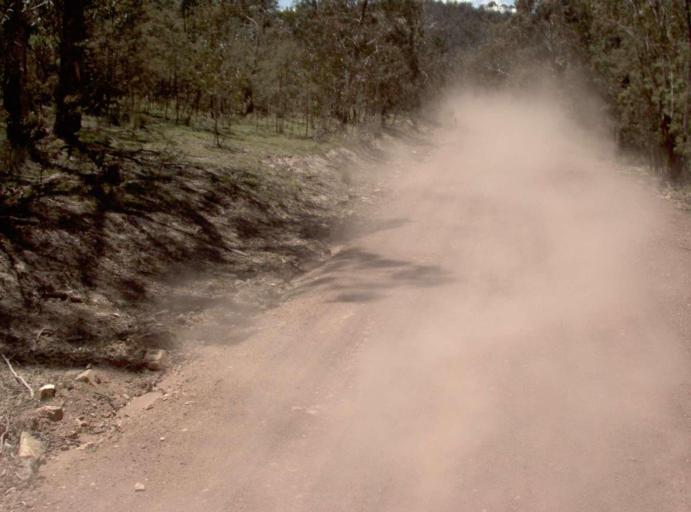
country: AU
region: New South Wales
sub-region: Snowy River
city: Jindabyne
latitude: -37.0647
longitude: 148.3184
